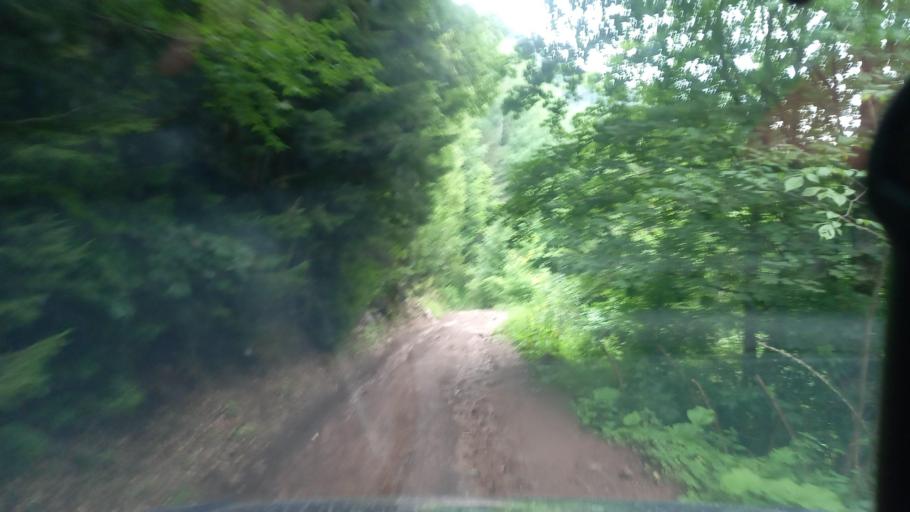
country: RU
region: Karachayevo-Cherkesiya
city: Kurdzhinovo
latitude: 43.8142
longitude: 40.8769
